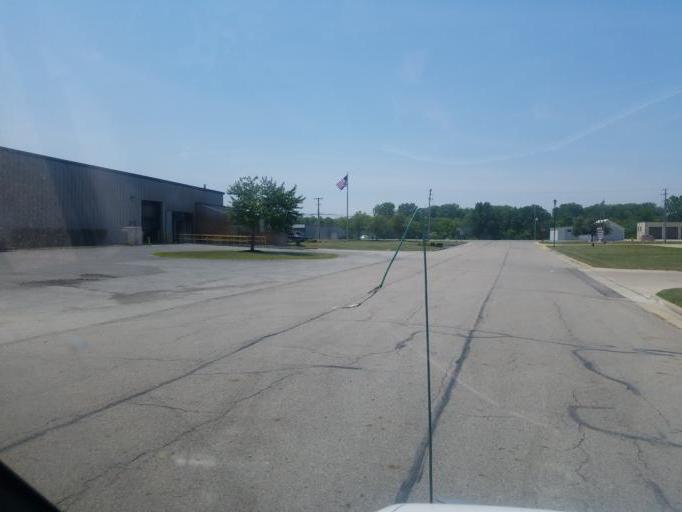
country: US
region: Ohio
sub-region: Shelby County
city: Fort Loramie
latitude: 40.3391
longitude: -84.3732
